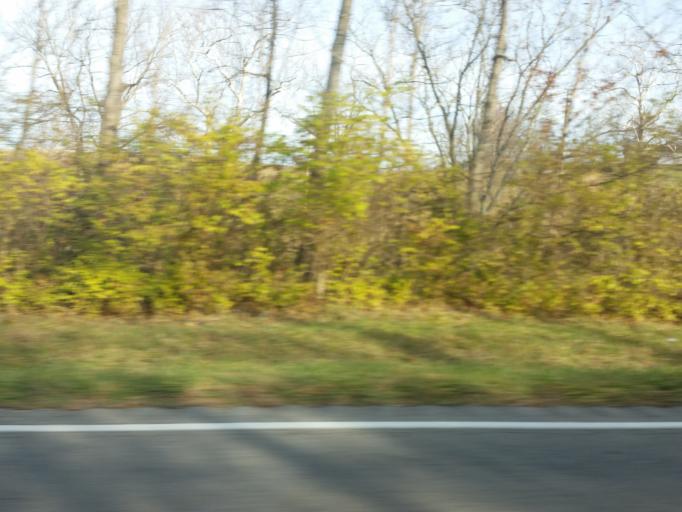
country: US
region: Kentucky
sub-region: Harrison County
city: Cynthiana
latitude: 38.4499
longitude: -84.2837
